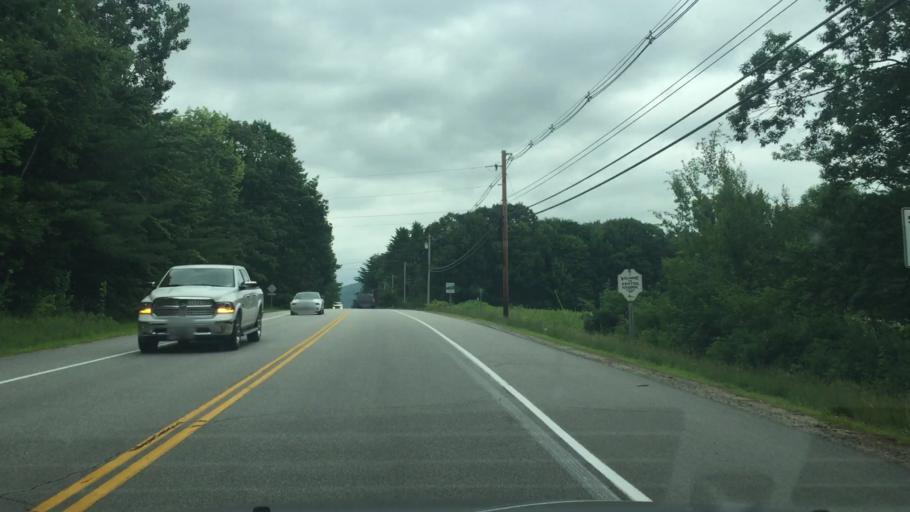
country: US
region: New Hampshire
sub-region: Carroll County
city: Center Harbor
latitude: 43.6886
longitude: -71.4582
